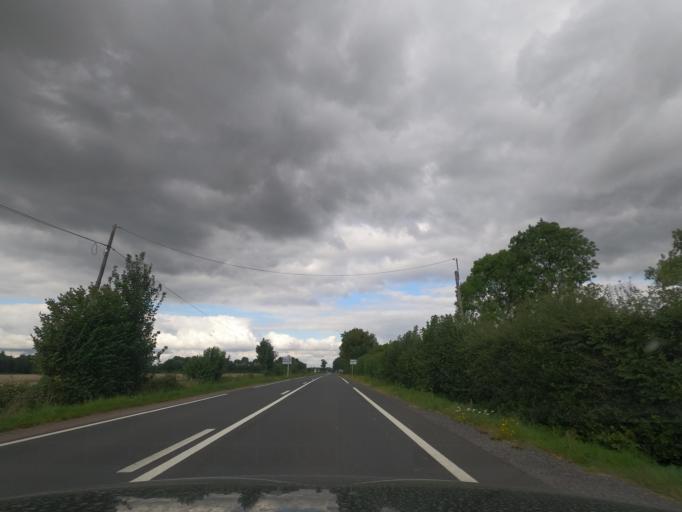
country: FR
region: Lower Normandy
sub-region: Departement de l'Orne
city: Gace
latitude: 48.8547
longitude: 0.3607
